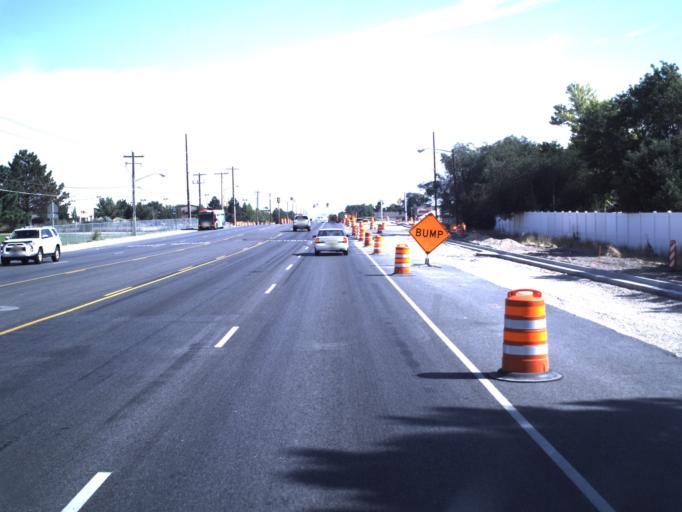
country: US
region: Utah
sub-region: Salt Lake County
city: West Valley City
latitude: 40.6798
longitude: -112.0247
